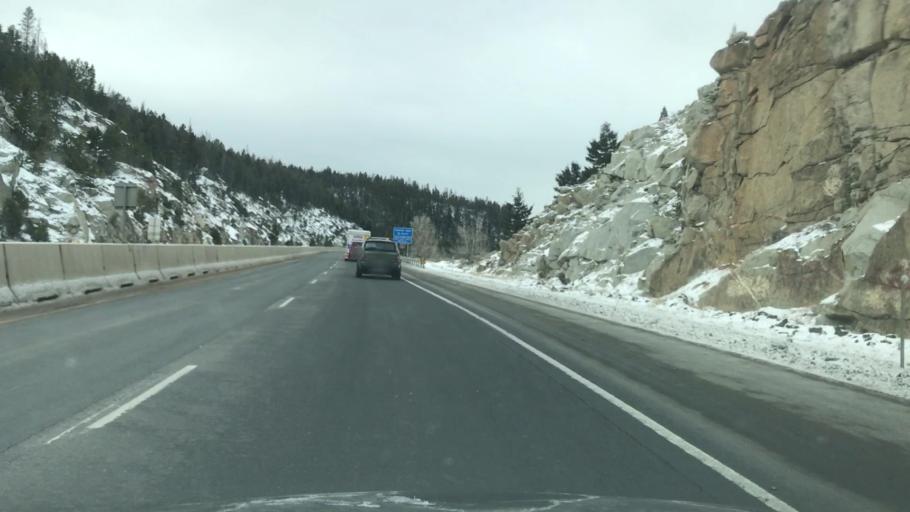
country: US
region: Montana
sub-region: Silver Bow County
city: Butte
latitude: 45.9119
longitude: -112.3338
